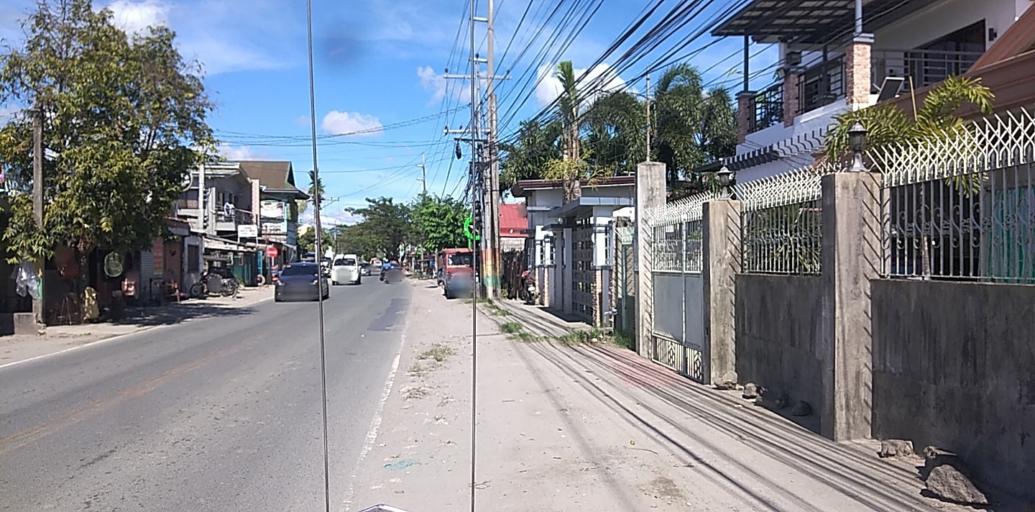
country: PH
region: Central Luzon
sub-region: Province of Pampanga
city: Arayat
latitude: 15.1261
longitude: 120.7758
